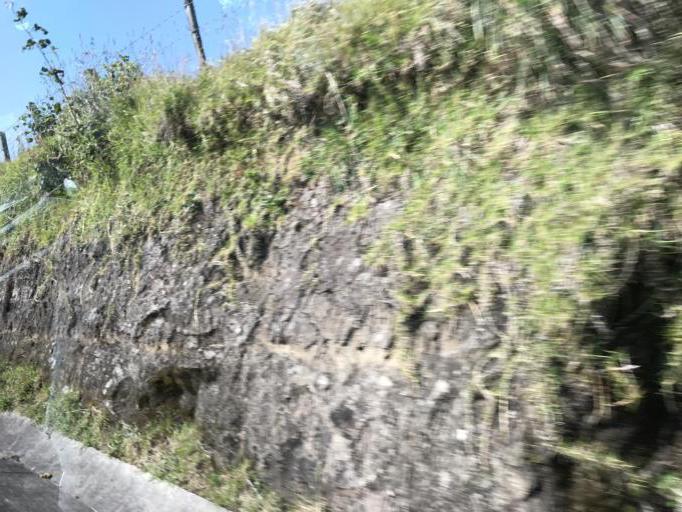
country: CO
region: Cauca
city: Paispamba
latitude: 2.2409
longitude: -76.4975
